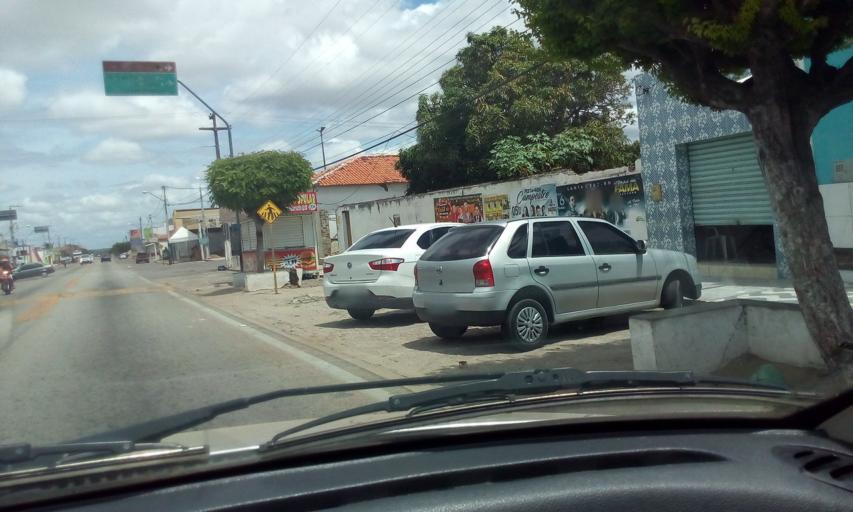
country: BR
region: Rio Grande do Norte
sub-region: Tangara
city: Tangara
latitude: -6.2001
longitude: -35.8014
